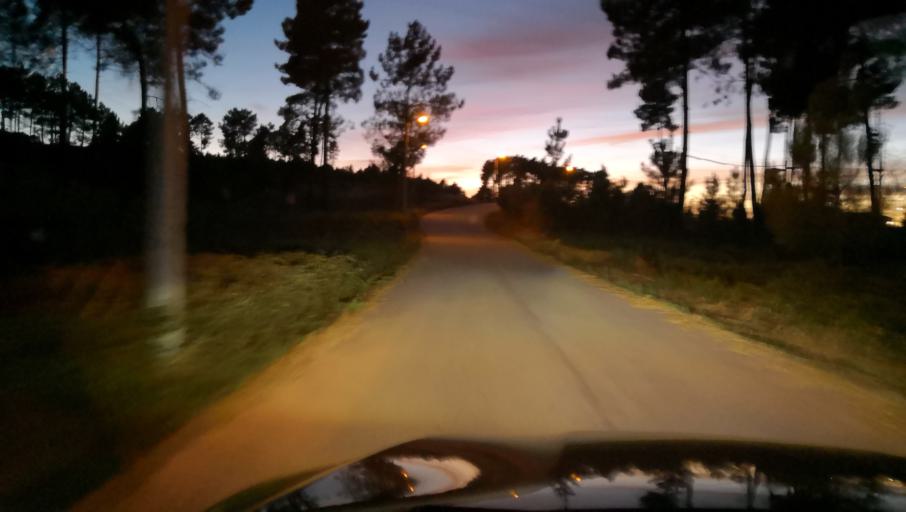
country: PT
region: Vila Real
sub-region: Sabrosa
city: Vilela
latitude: 41.2553
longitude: -7.6497
